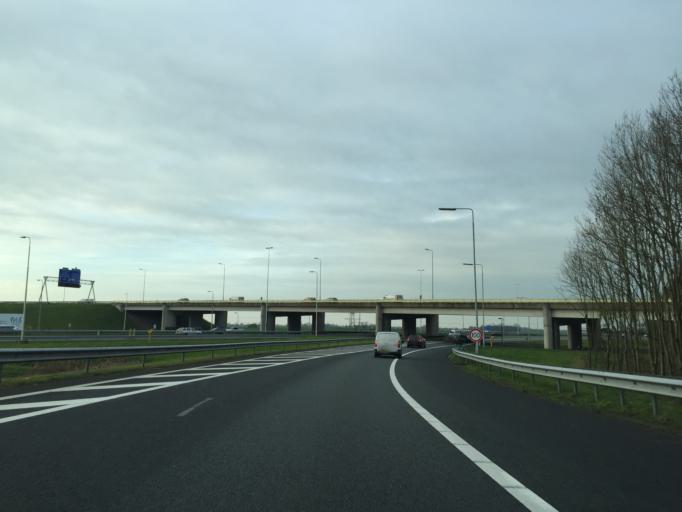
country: NL
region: Utrecht
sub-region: Gemeente Nieuwegein
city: Nieuwegein
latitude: 52.0674
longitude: 5.0673
